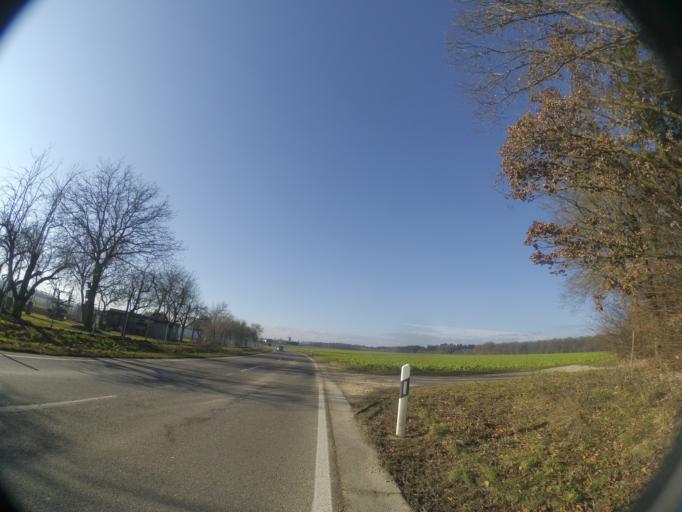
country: DE
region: Baden-Wuerttemberg
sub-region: Tuebingen Region
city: Dornstadt
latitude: 48.4743
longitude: 9.9623
